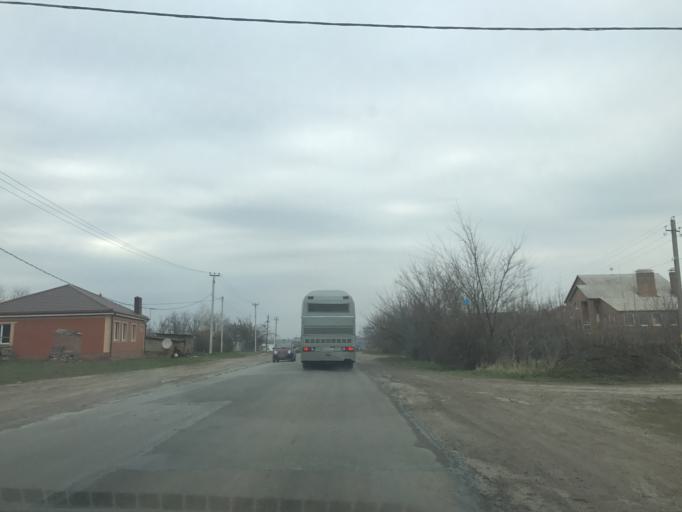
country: RU
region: Rostov
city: Novocherkassk
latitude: 47.3962
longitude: 40.0648
